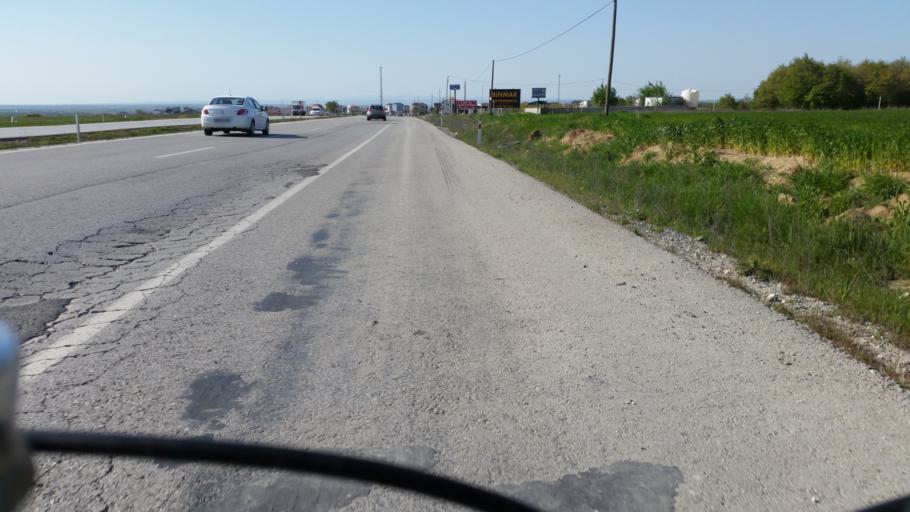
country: TR
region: Tekirdag
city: Cerkezkoey
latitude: 41.3479
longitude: 27.9597
